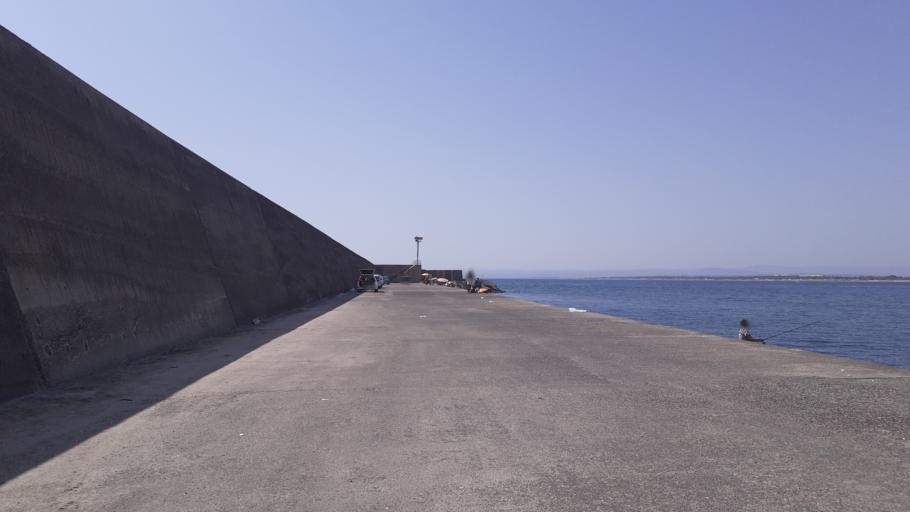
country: IT
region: Sicily
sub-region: Catania
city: Catania
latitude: 37.4858
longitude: 15.0993
